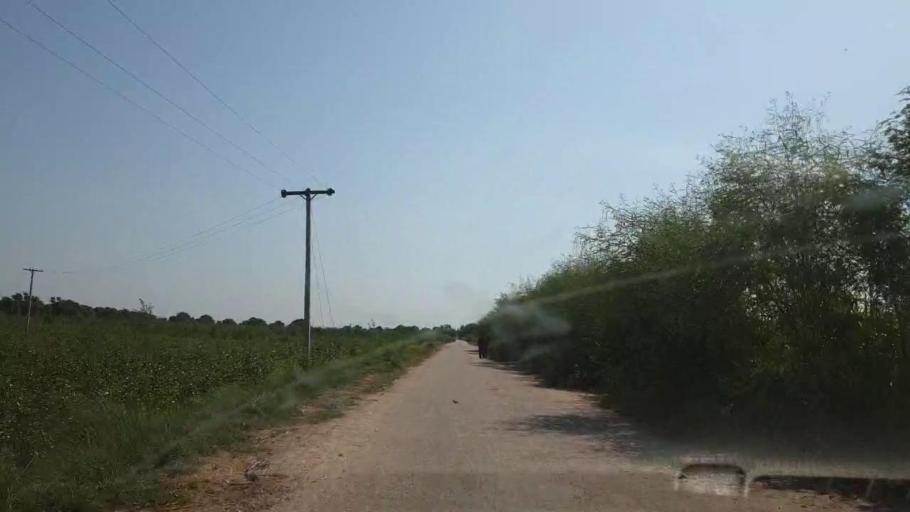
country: PK
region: Sindh
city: Tando Jam
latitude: 25.4304
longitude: 68.5819
